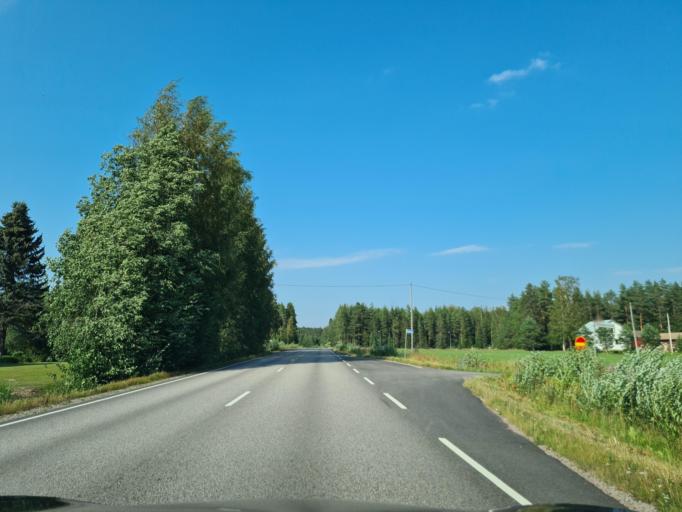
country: FI
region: Satakunta
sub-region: Pohjois-Satakunta
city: Karvia
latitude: 62.2219
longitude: 22.6110
